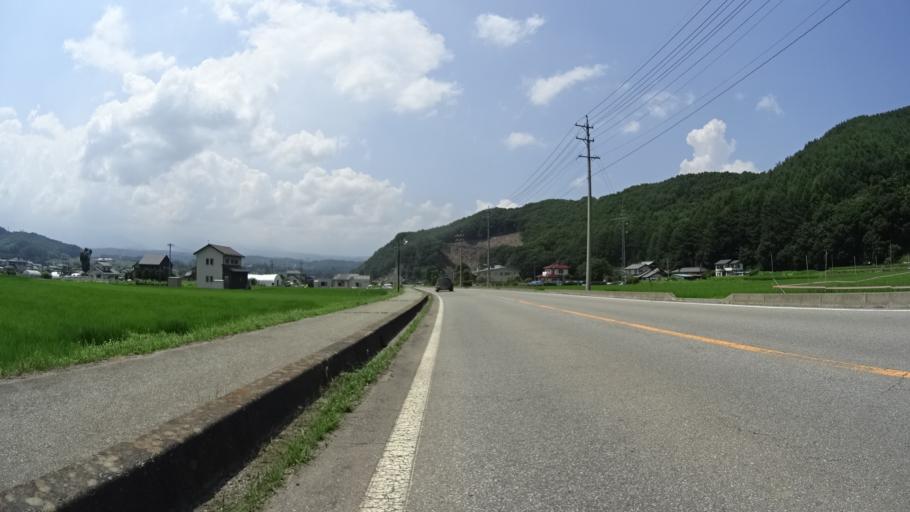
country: JP
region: Nagano
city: Saku
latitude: 36.1542
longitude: 138.5026
